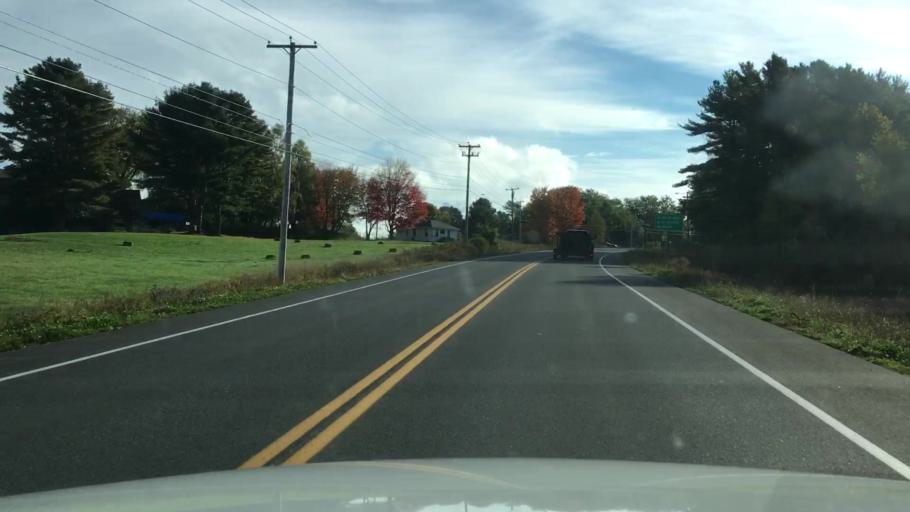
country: US
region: Maine
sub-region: Knox County
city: Thomaston
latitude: 44.0774
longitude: -69.2063
